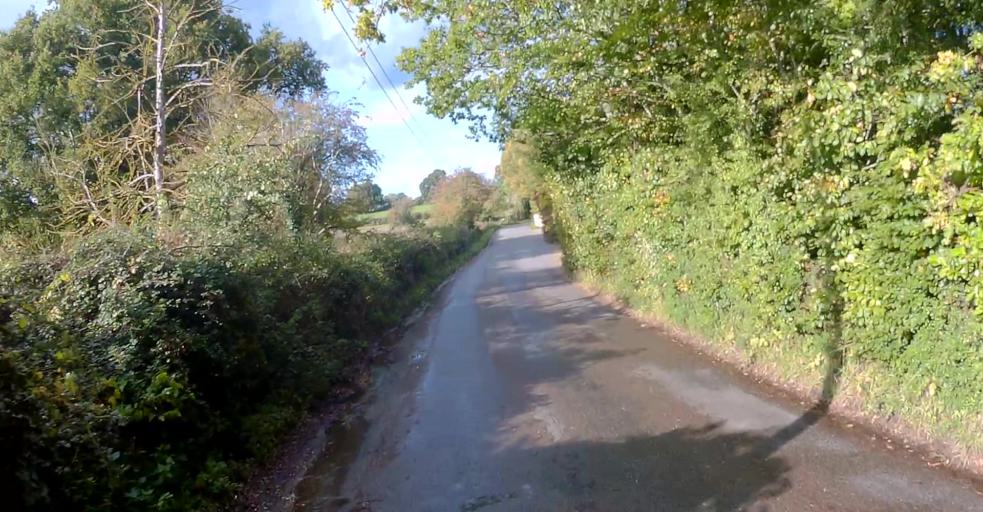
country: GB
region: England
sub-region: Surrey
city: Farnham
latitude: 51.2042
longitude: -0.8266
